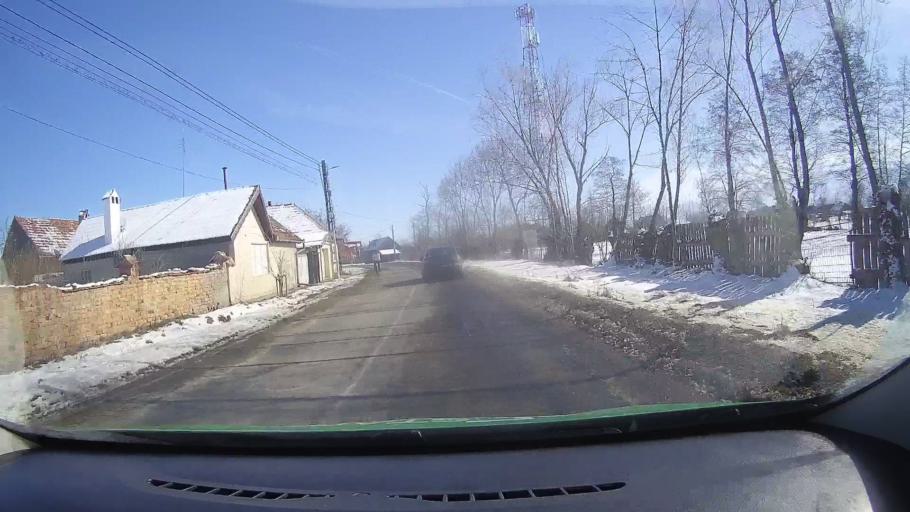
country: RO
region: Brasov
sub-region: Comuna Recea
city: Recea
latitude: 45.7286
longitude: 24.9068
